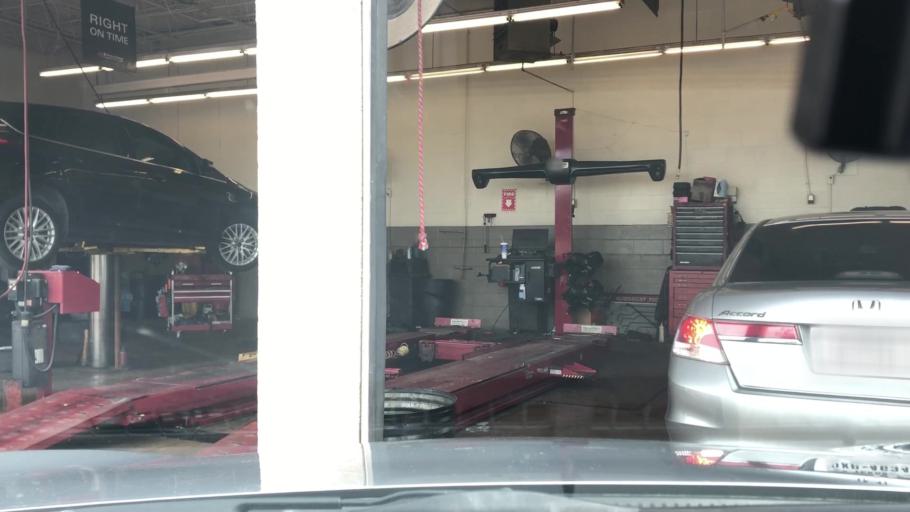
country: US
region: Texas
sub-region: Bexar County
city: Universal City
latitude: 29.5543
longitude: -98.3103
